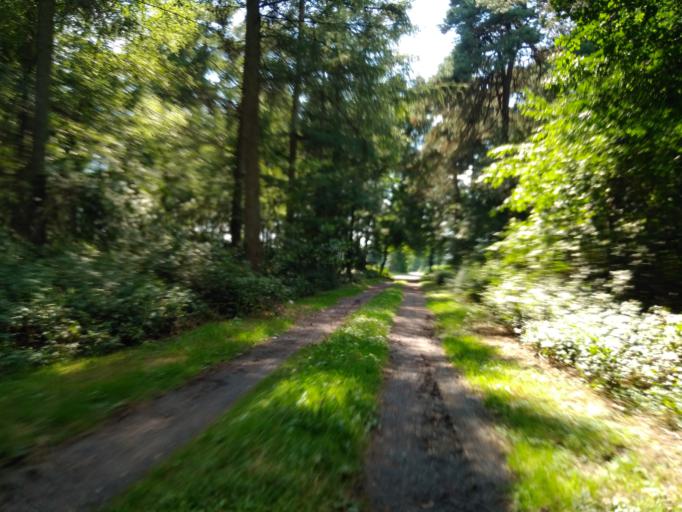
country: DE
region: North Rhine-Westphalia
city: Dorsten
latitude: 51.7414
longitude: 6.9667
